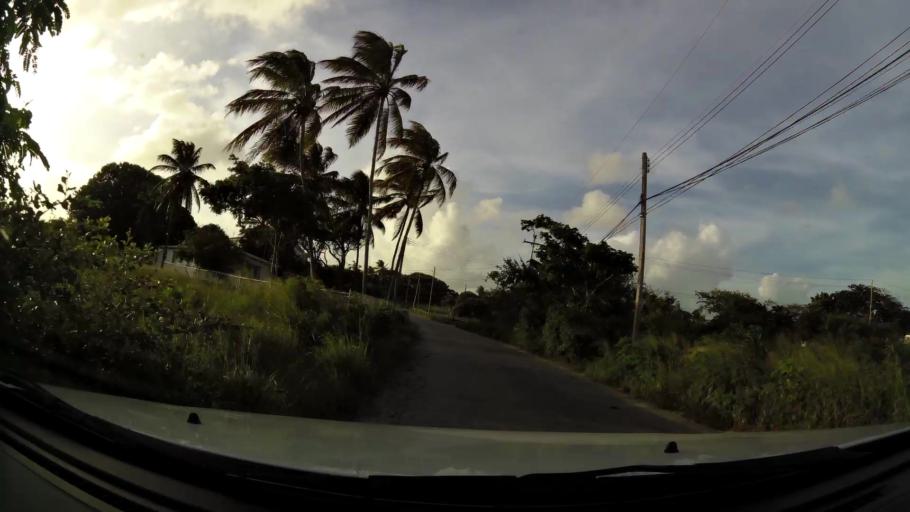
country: BB
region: Christ Church
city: Oistins
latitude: 13.0744
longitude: -59.5112
